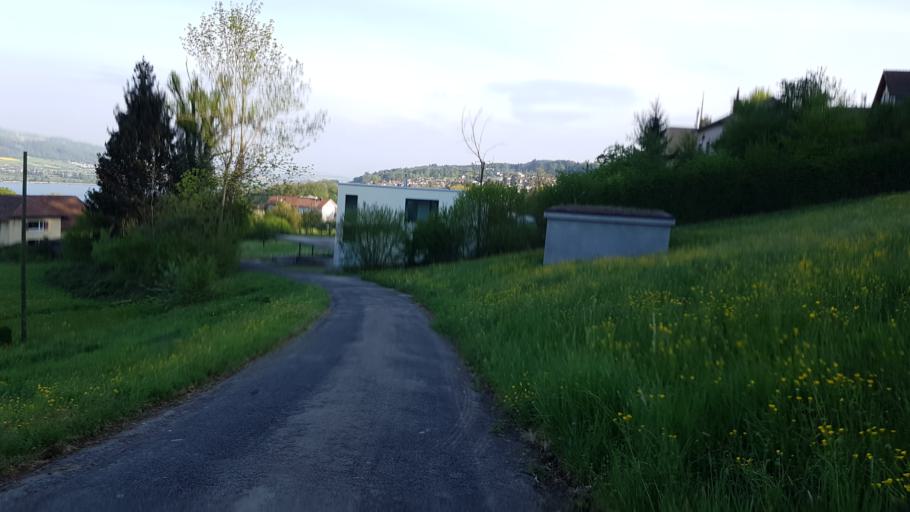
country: CH
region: Aargau
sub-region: Bezirk Kulm
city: Reinach
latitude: 47.2745
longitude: 8.1997
